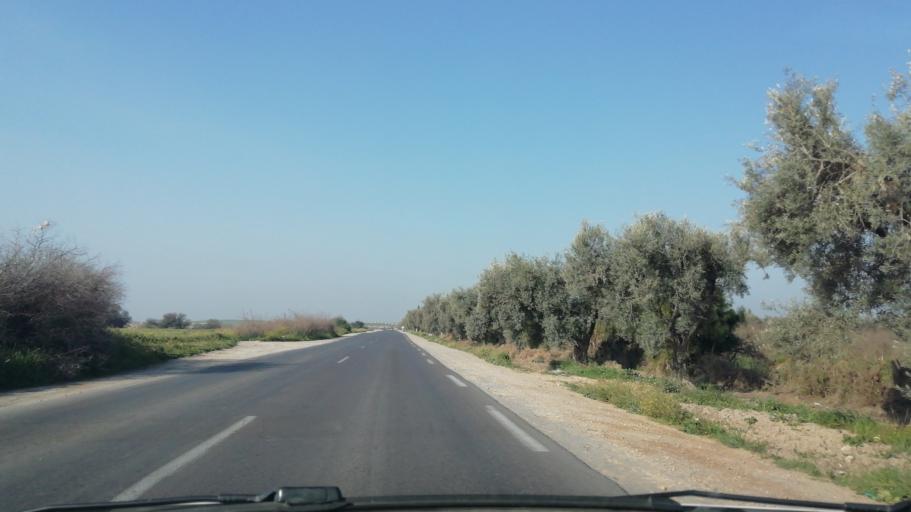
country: DZ
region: Mostaganem
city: Mostaganem
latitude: 35.7458
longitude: 0.1535
